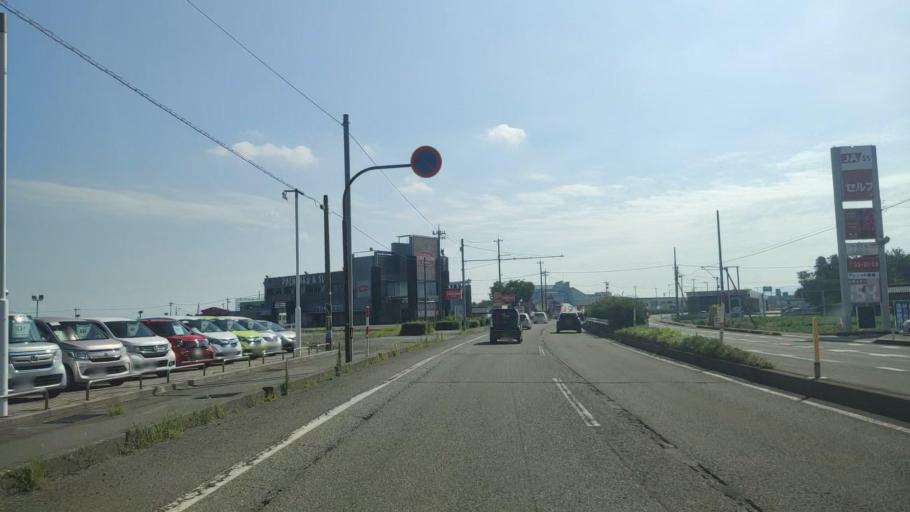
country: JP
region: Ishikawa
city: Matsuto
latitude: 36.5079
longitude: 136.5557
